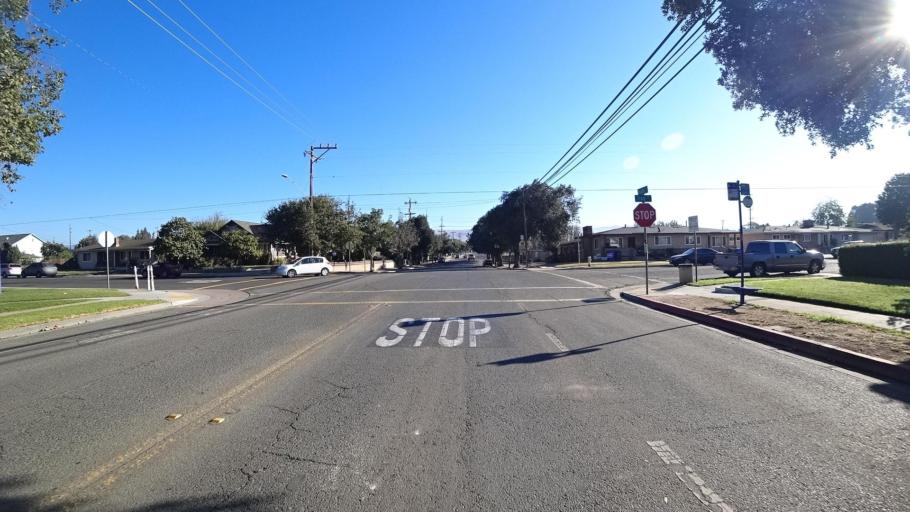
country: US
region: California
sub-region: Monterey County
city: Gonzales
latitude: 36.5095
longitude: -121.4430
